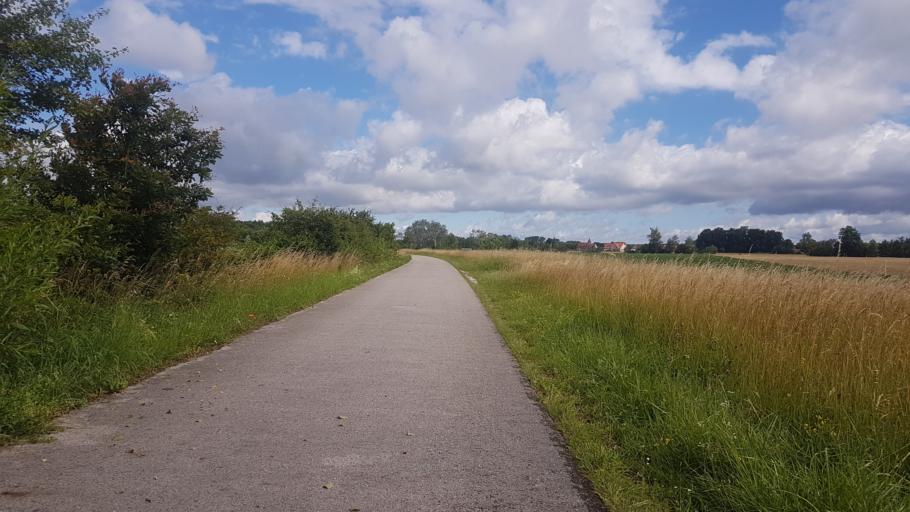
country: DE
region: Bavaria
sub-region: Regierungsbezirk Mittelfranken
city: Ornbau
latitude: 49.1611
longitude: 10.6600
